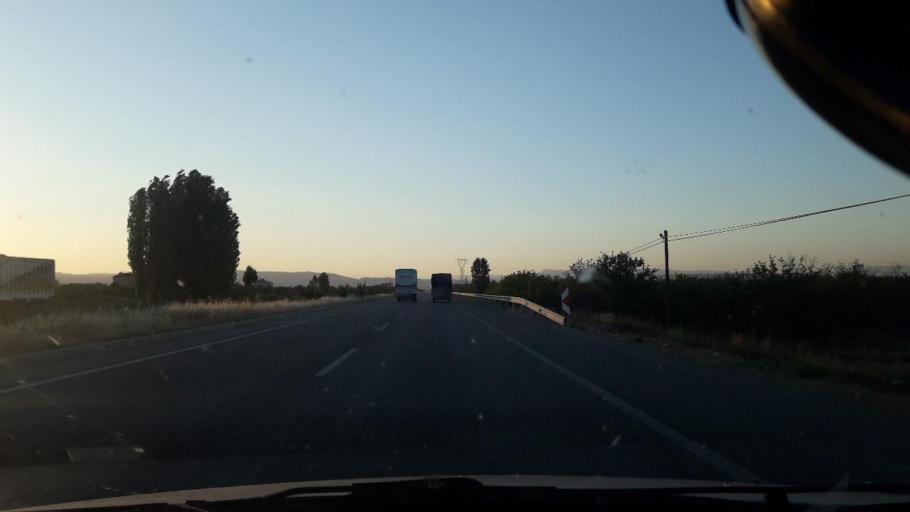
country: TR
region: Malatya
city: Yazihan
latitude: 38.4755
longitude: 38.2222
